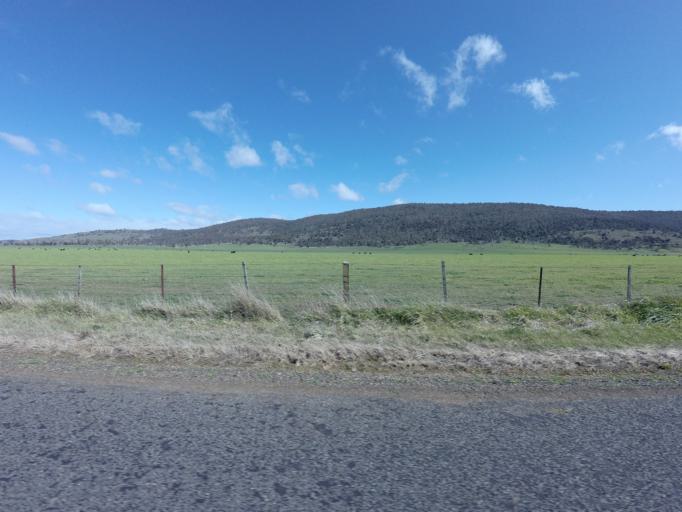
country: AU
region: Tasmania
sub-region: Northern Midlands
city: Evandale
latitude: -41.9761
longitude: 147.4459
